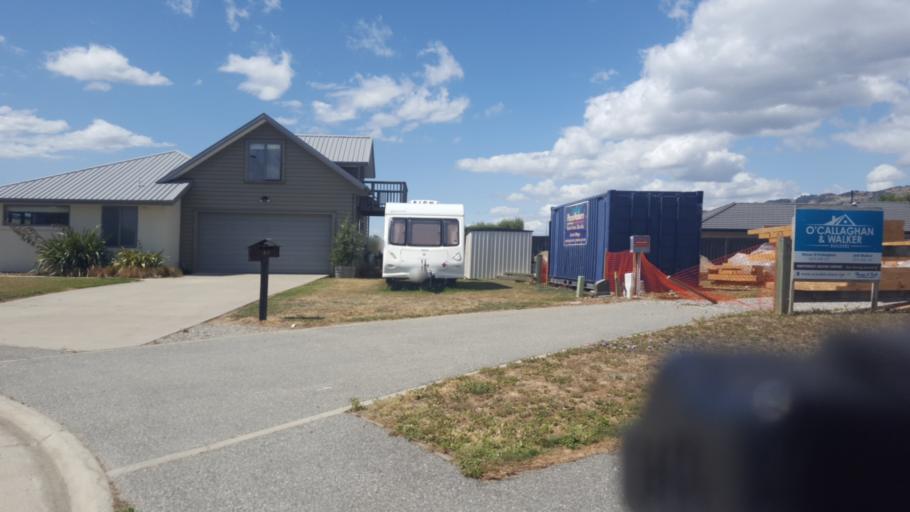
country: NZ
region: Otago
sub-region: Queenstown-Lakes District
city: Wanaka
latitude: -44.9714
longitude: 169.2491
